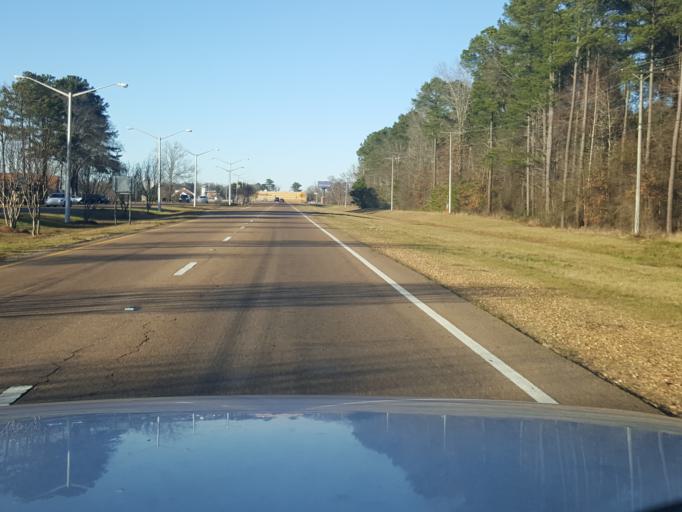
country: US
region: Mississippi
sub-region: Rankin County
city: Flowood
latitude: 32.3307
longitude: -90.0909
